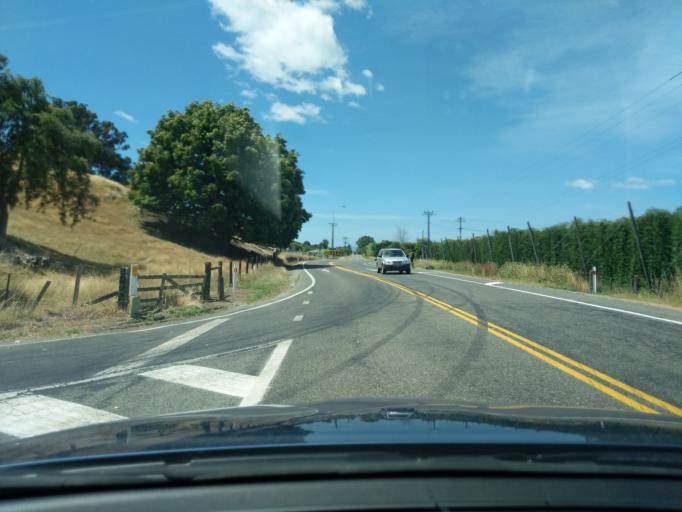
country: NZ
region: Tasman
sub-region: Tasman District
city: Motueka
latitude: -41.0629
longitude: 172.9837
